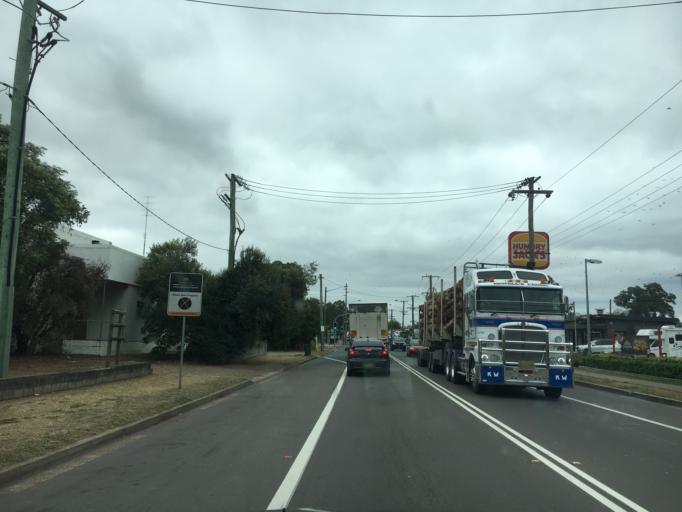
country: AU
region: New South Wales
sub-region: Singleton
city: Singleton
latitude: -32.5701
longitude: 151.1807
